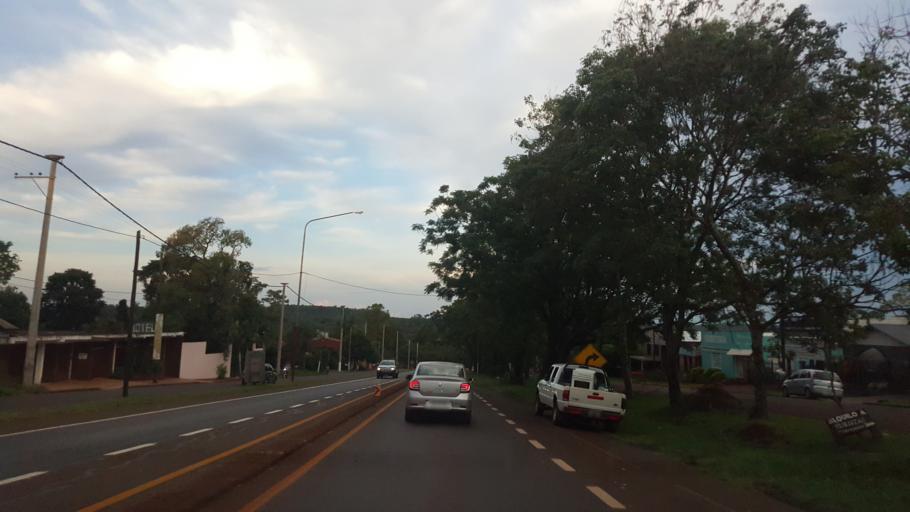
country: AR
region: Misiones
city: Jardin America
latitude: -27.0352
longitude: -55.2251
